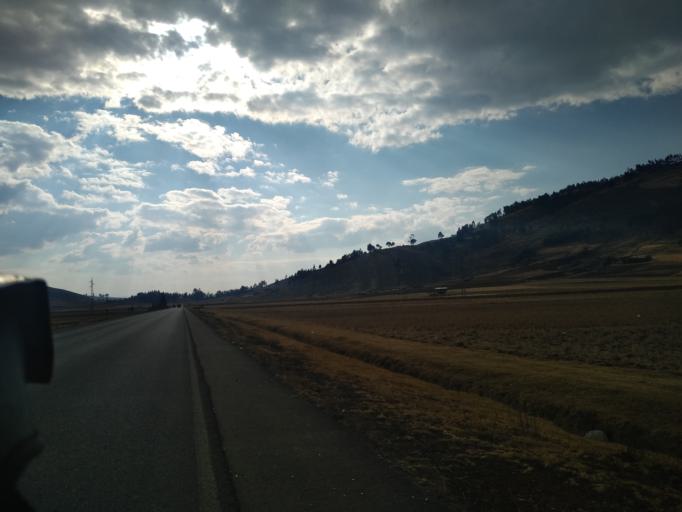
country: PE
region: Cajamarca
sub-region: Provincia de Cajamarca
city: Encanada
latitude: -7.1392
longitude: -78.3805
